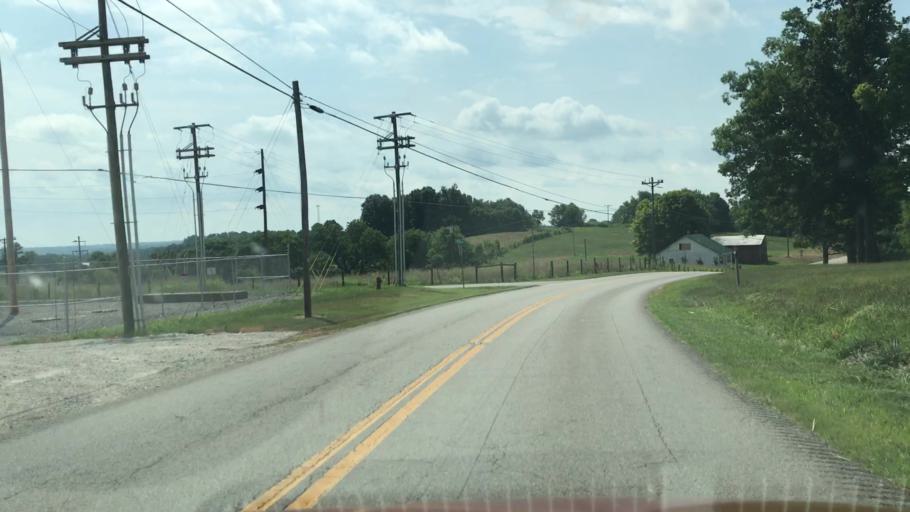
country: US
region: Kentucky
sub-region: Barren County
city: Glasgow
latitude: 36.8972
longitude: -85.8580
